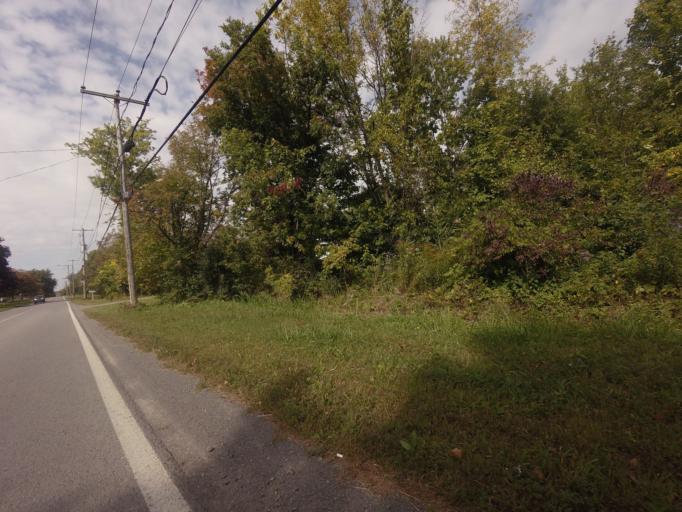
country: CA
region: Quebec
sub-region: Laurentides
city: Blainville
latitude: 45.6194
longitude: -73.9071
